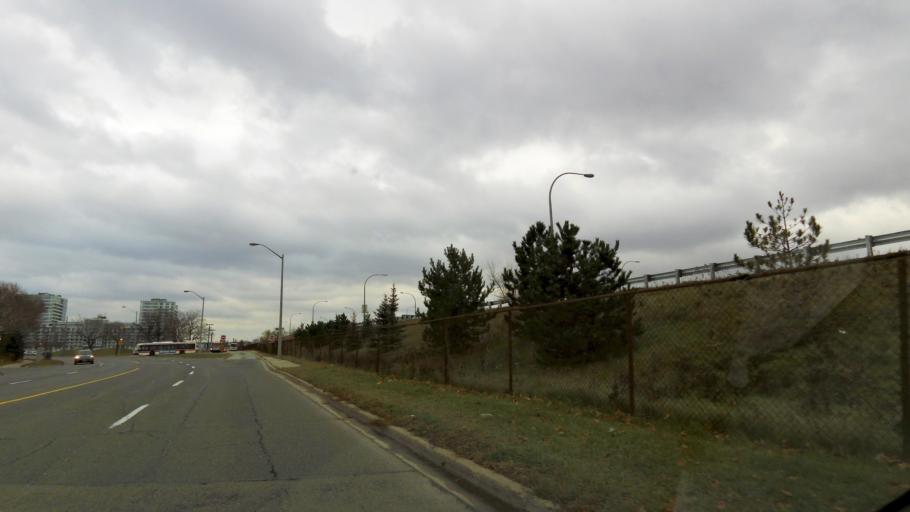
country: CA
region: Ontario
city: North York
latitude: 43.7379
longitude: -79.4507
